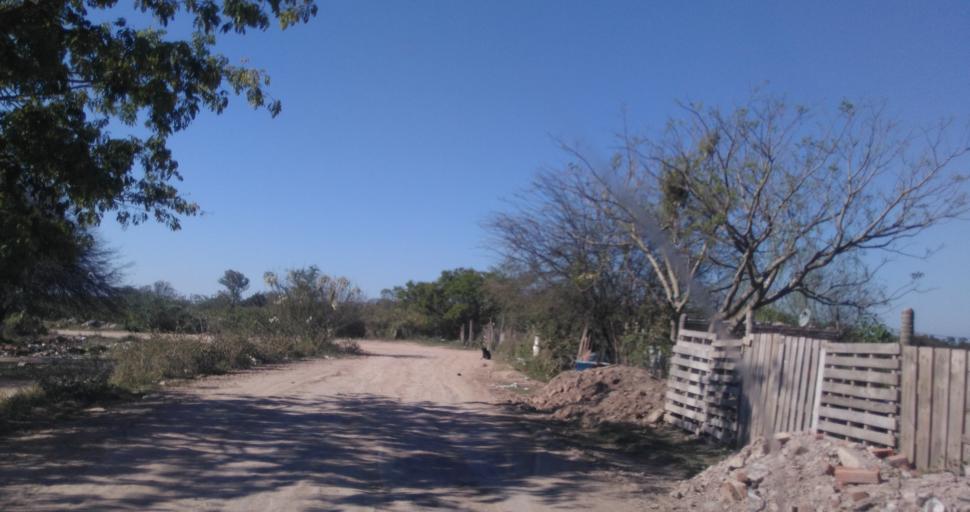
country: AR
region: Chaco
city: Resistencia
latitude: -27.4472
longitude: -58.9629
